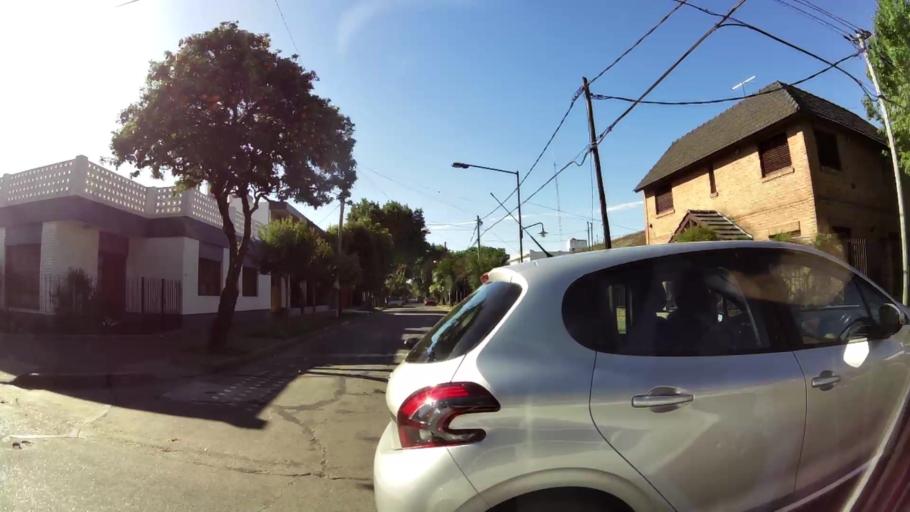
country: AR
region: Buenos Aires
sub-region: Partido de San Isidro
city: San Isidro
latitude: -34.4750
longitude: -58.5251
